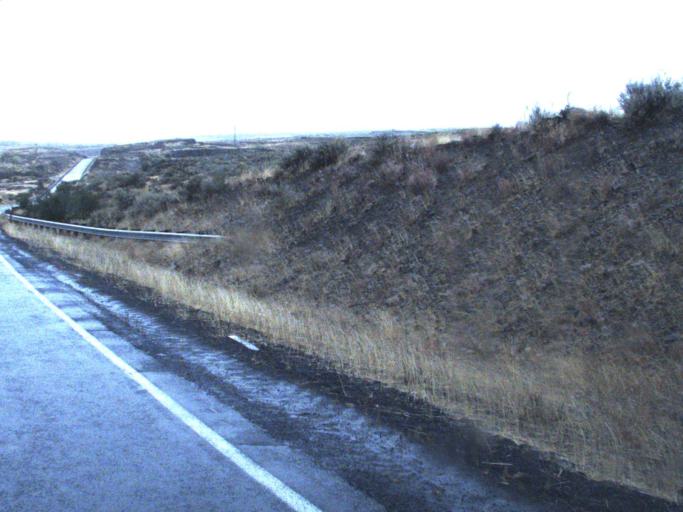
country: US
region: Washington
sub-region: Lincoln County
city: Davenport
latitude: 47.3527
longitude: -118.1012
